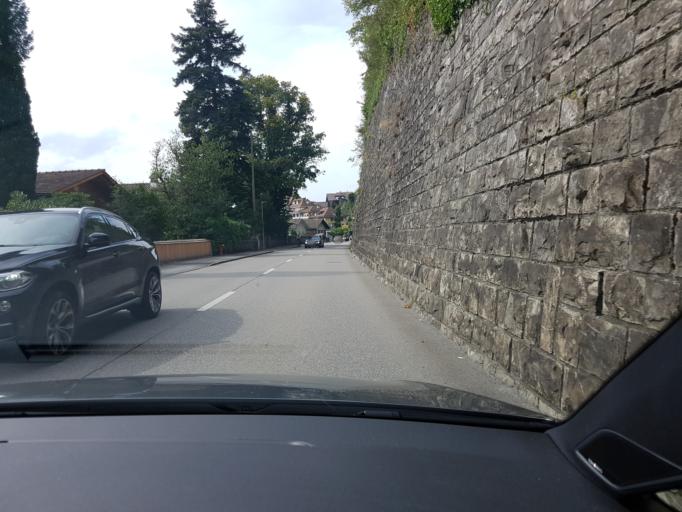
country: CH
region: Bern
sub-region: Thun District
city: Sigriswil
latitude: 46.7136
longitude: 7.6989
